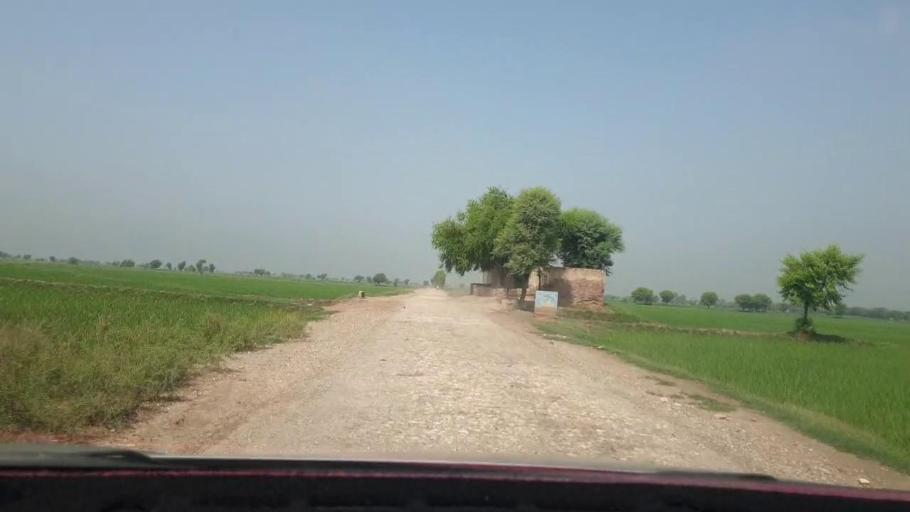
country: PK
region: Sindh
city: Nasirabad
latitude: 27.4302
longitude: 67.8664
